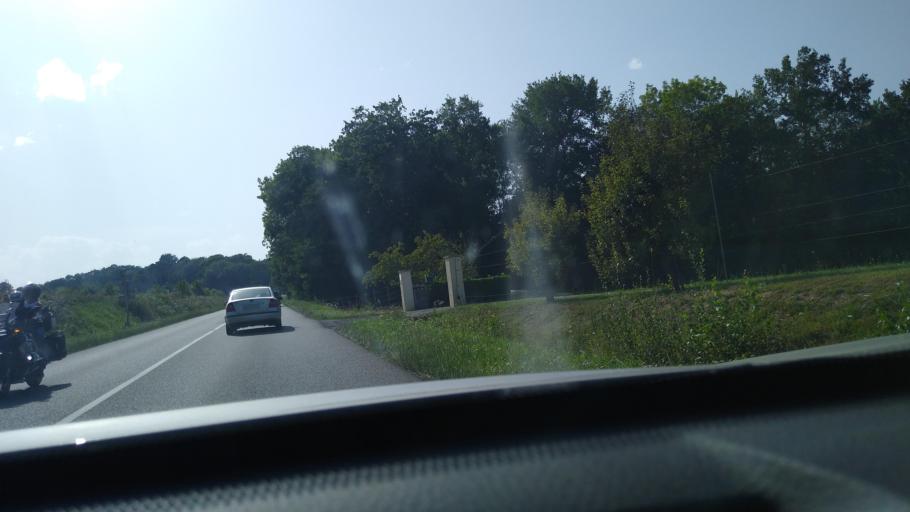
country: FR
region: Midi-Pyrenees
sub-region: Departement de la Haute-Garonne
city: Salies-du-Salat
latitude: 43.1024
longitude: 0.9482
